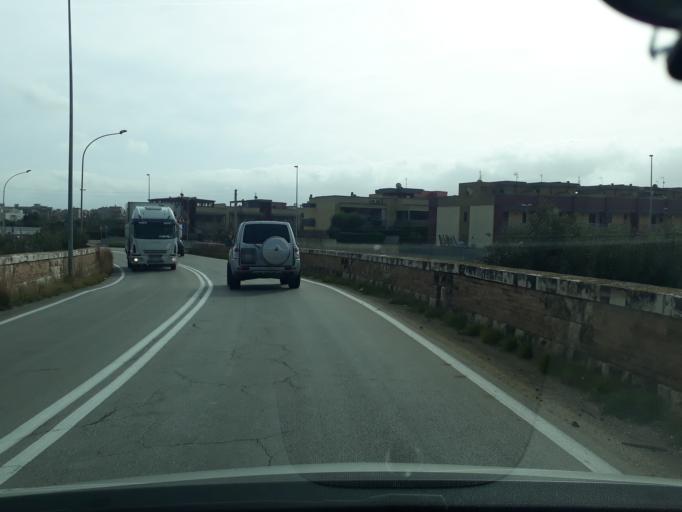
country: IT
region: Apulia
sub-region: Provincia di Bari
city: Monopoli
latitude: 40.9557
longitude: 17.2820
